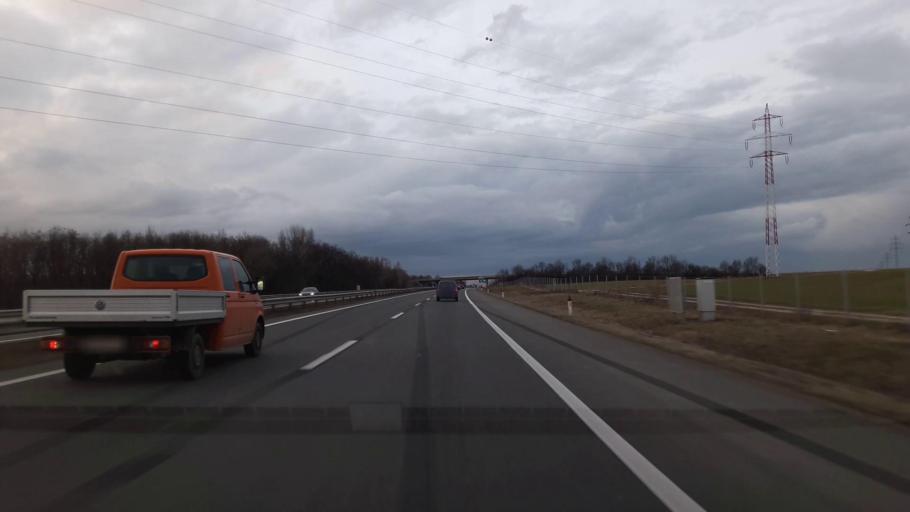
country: AT
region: Burgenland
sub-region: Eisenstadt-Umgebung
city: Steinbrunn
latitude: 47.8531
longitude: 16.4264
